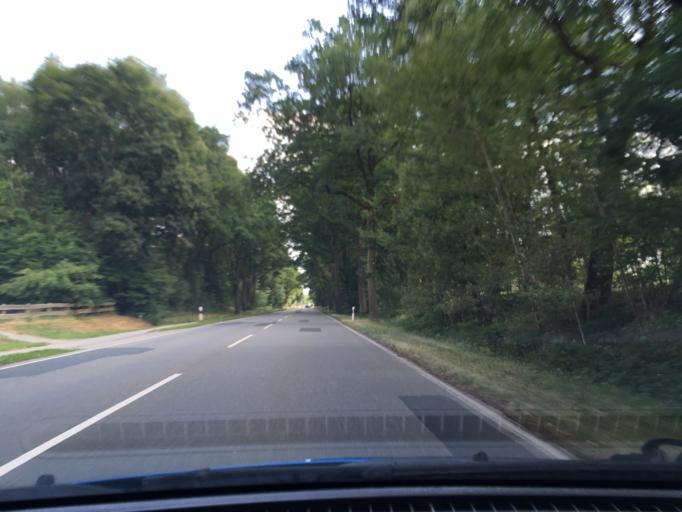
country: DE
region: Lower Saxony
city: Welle
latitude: 53.2588
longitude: 9.8054
